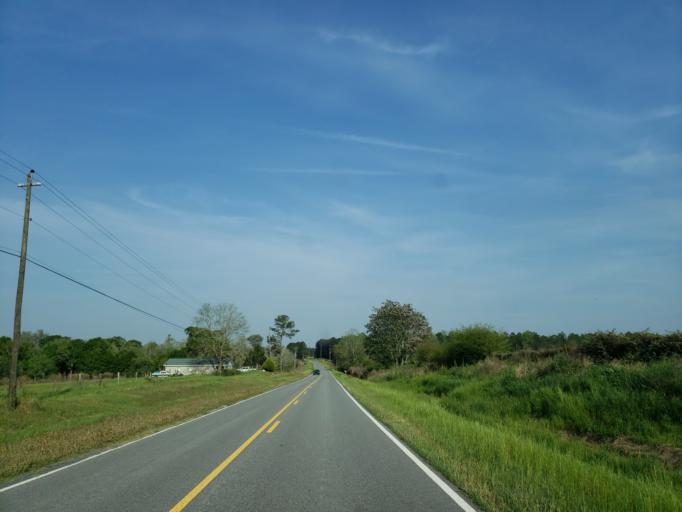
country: US
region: Georgia
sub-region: Tift County
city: Tifton
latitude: 31.5713
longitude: -83.5339
